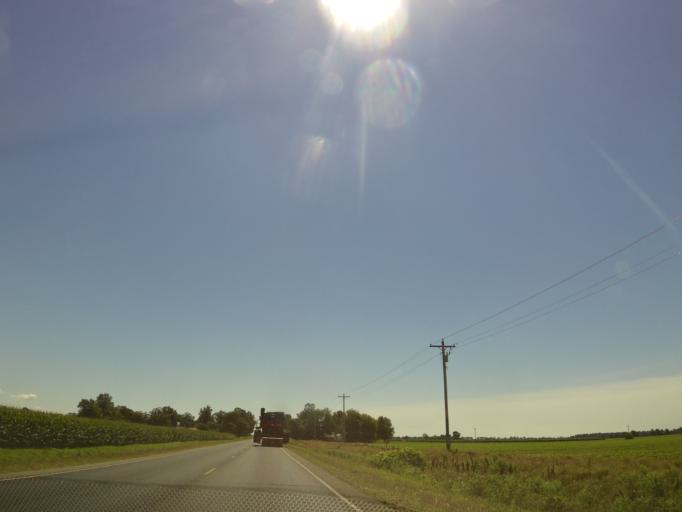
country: US
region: Missouri
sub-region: New Madrid County
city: Portageville
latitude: 36.5534
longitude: -89.7936
